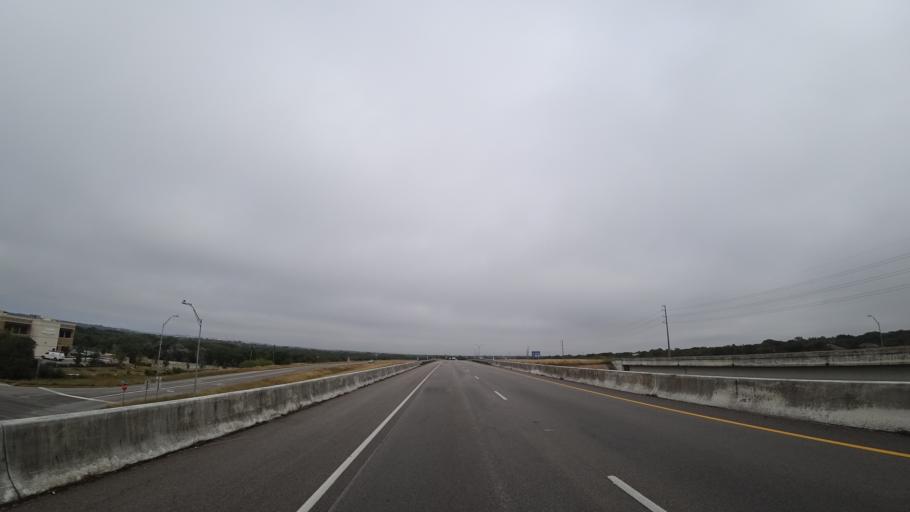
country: US
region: Texas
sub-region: Travis County
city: Shady Hollow
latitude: 30.2082
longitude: -97.8613
